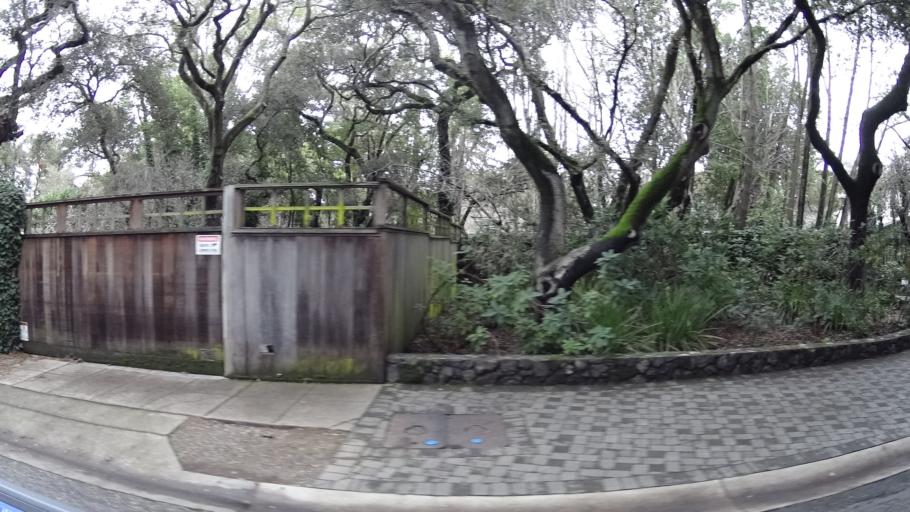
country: US
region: California
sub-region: San Mateo County
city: Burlingame
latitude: 37.5669
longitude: -122.3515
